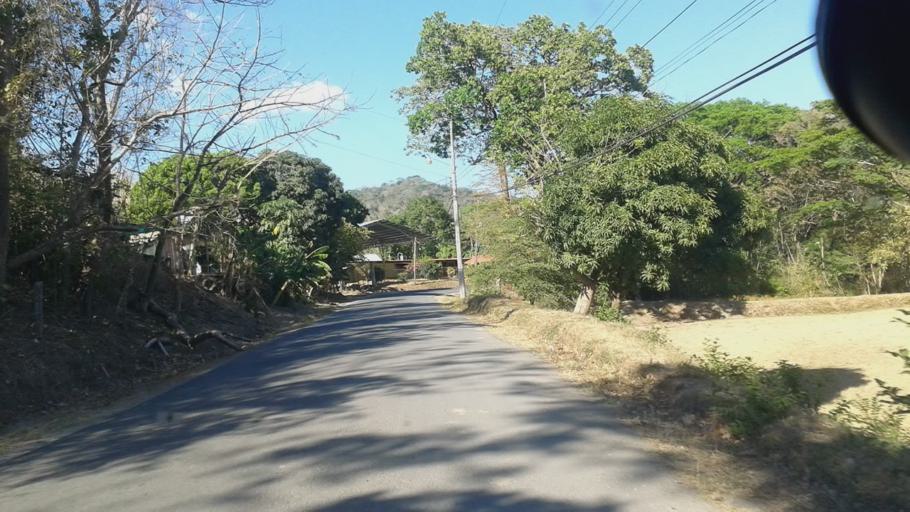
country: CR
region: Guanacaste
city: Samara
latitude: 9.9203
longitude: -85.5365
